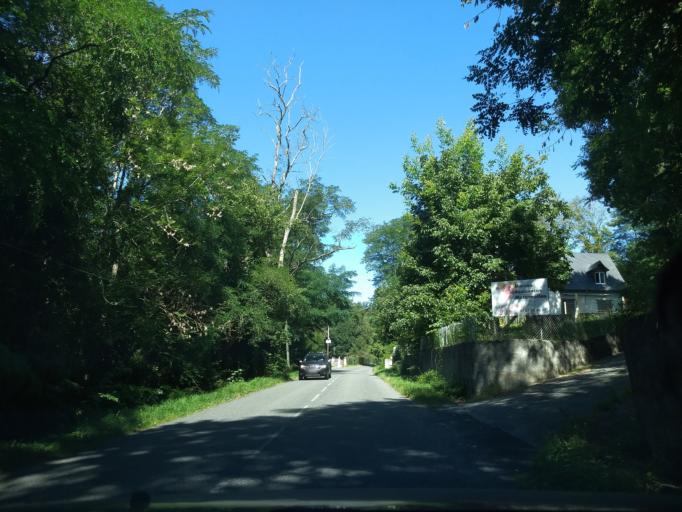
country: FR
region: Aquitaine
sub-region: Departement des Pyrenees-Atlantiques
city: Soumoulou
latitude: 43.2718
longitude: -0.1862
